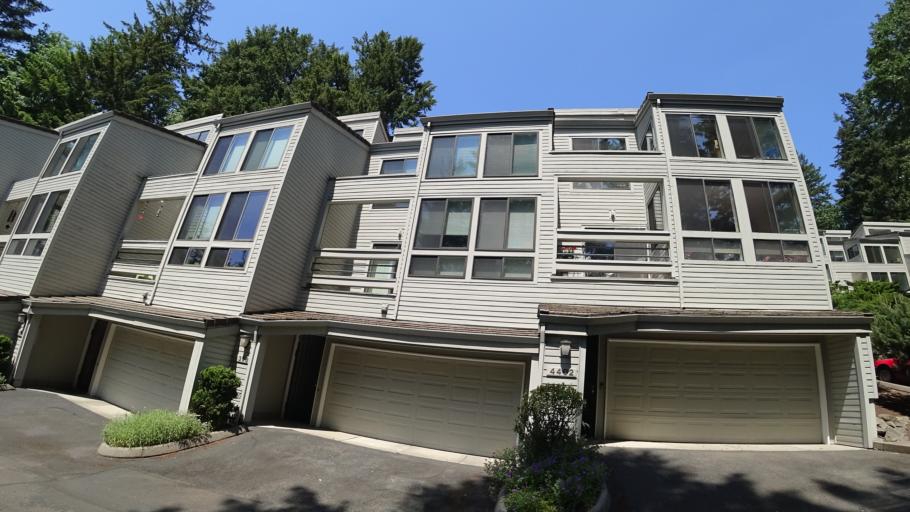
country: US
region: Oregon
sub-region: Washington County
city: Durham
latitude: 45.4268
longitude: -122.7215
